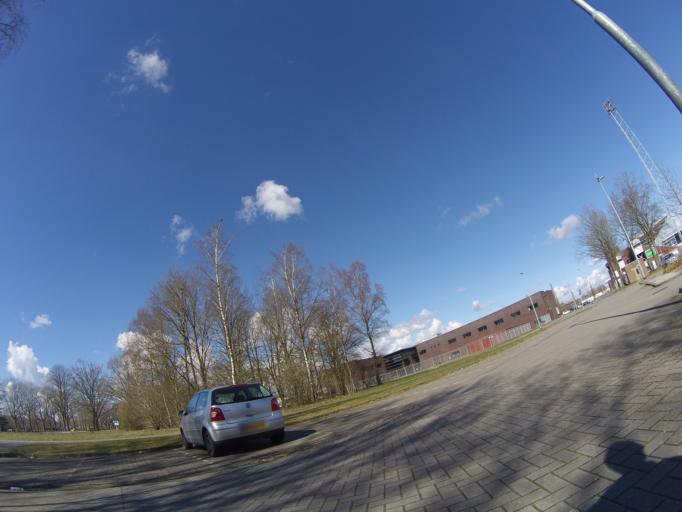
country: NL
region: Drenthe
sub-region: Gemeente Emmen
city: Emmen
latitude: 52.7732
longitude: 6.9451
